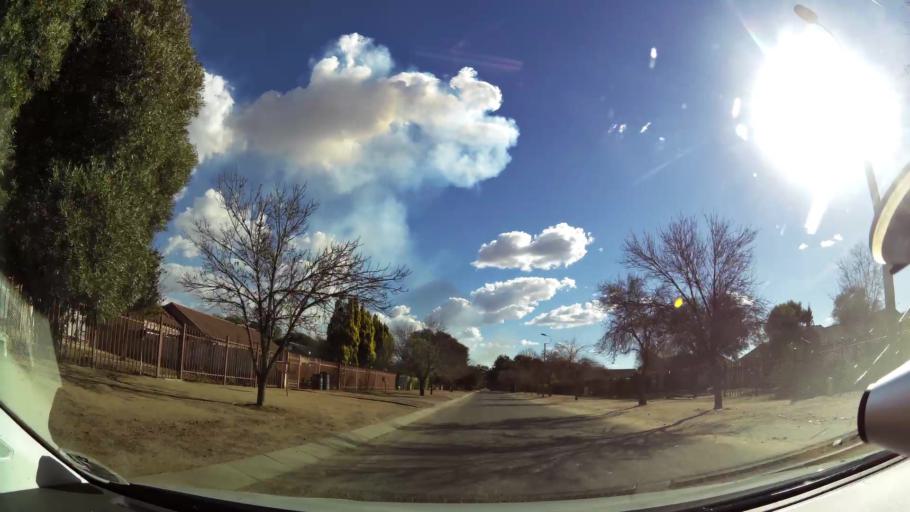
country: ZA
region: North-West
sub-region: Dr Kenneth Kaunda District Municipality
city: Klerksdorp
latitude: -26.8215
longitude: 26.6637
